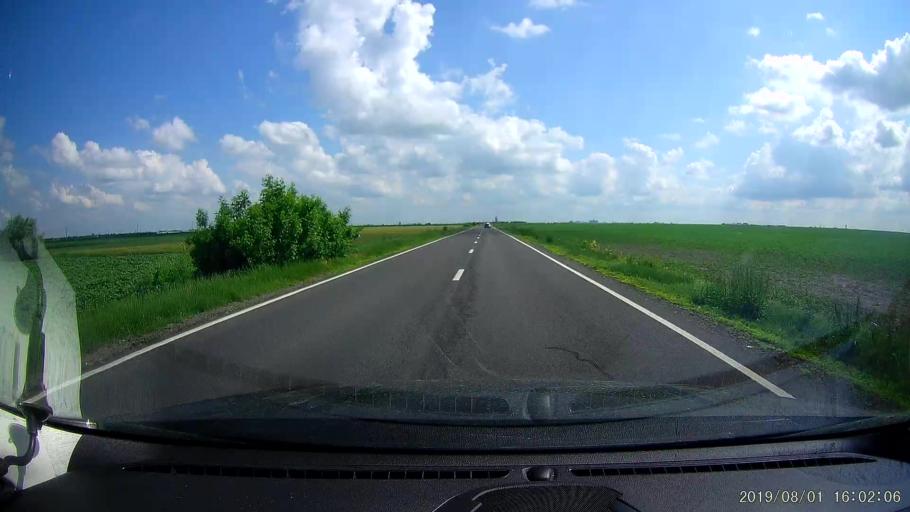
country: RO
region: Ialomita
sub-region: Comuna Ciulnita
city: Ciulnita
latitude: 44.4964
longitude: 27.3884
